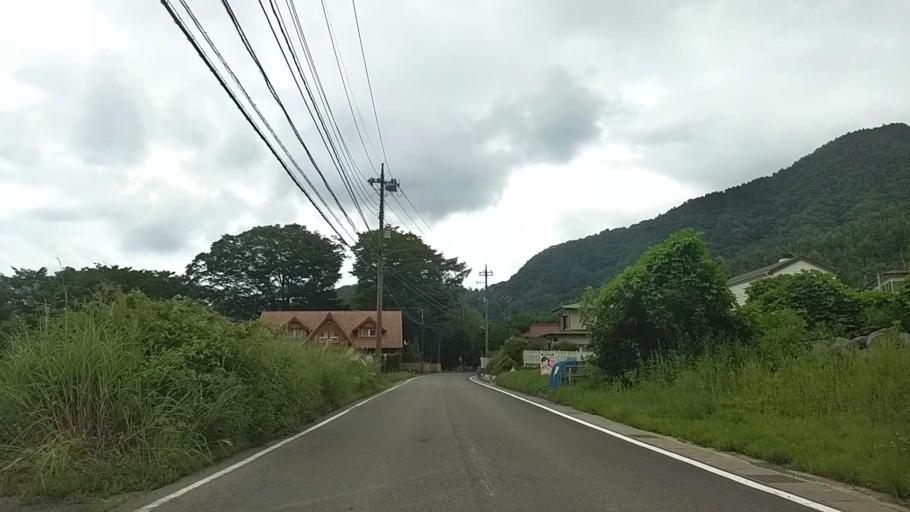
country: JP
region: Yamanashi
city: Fujikawaguchiko
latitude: 35.5043
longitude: 138.7182
